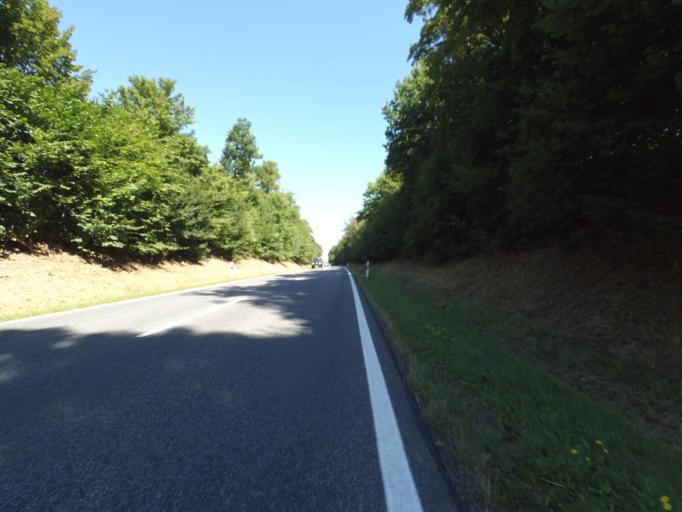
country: DE
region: Rheinland-Pfalz
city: Alflen
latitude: 50.1655
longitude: 7.0395
